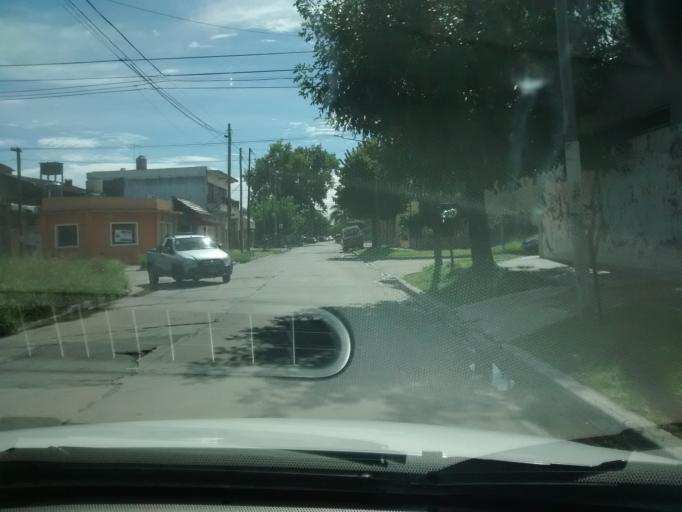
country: AR
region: Buenos Aires
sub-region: Partido de Moron
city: Moron
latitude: -34.6664
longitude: -58.6093
